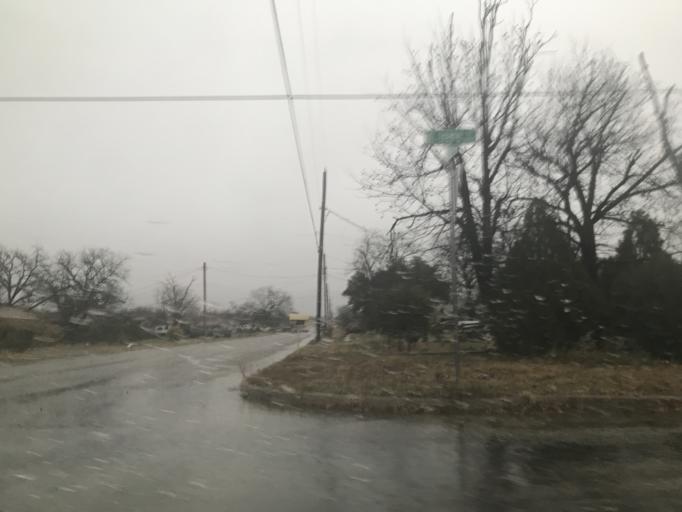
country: US
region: Texas
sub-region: Tom Green County
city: San Angelo
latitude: 31.4693
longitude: -100.4175
